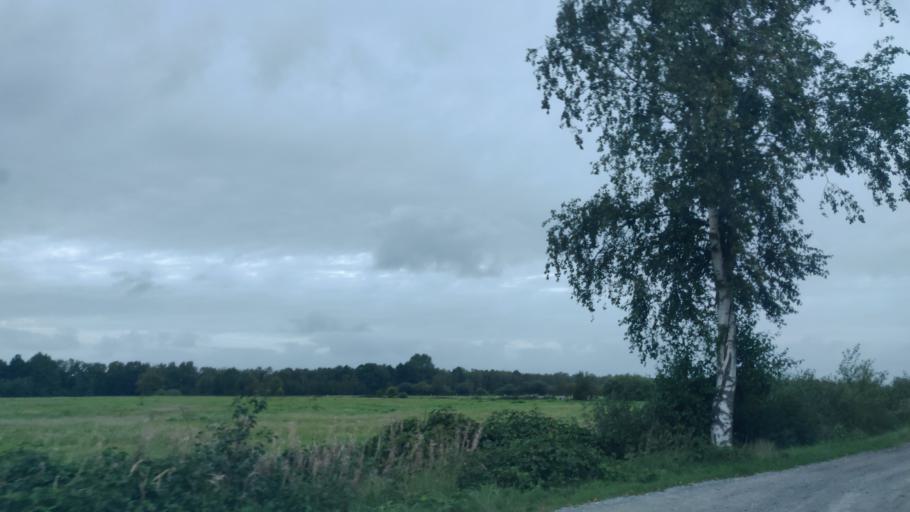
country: DE
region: Lower Saxony
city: Aurich
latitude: 53.5318
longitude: 7.4715
